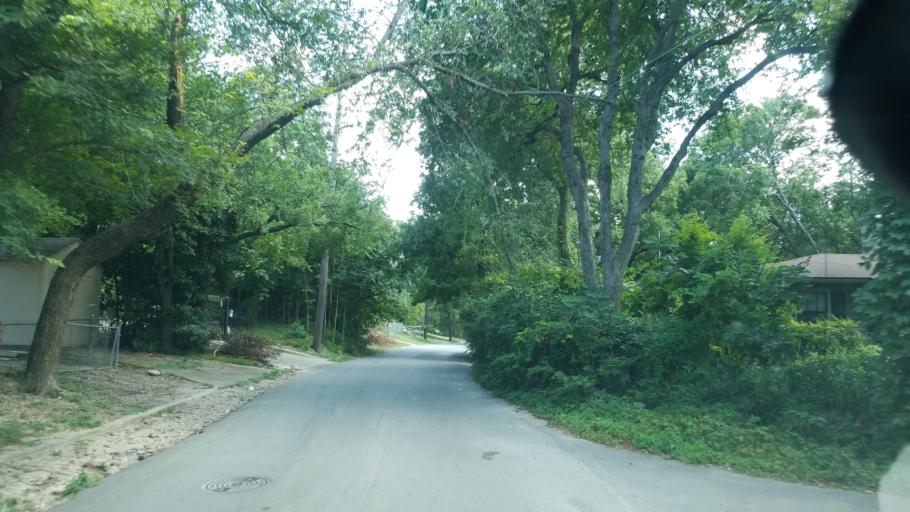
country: US
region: Texas
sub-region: Dallas County
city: Balch Springs
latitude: 32.7662
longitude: -96.6971
